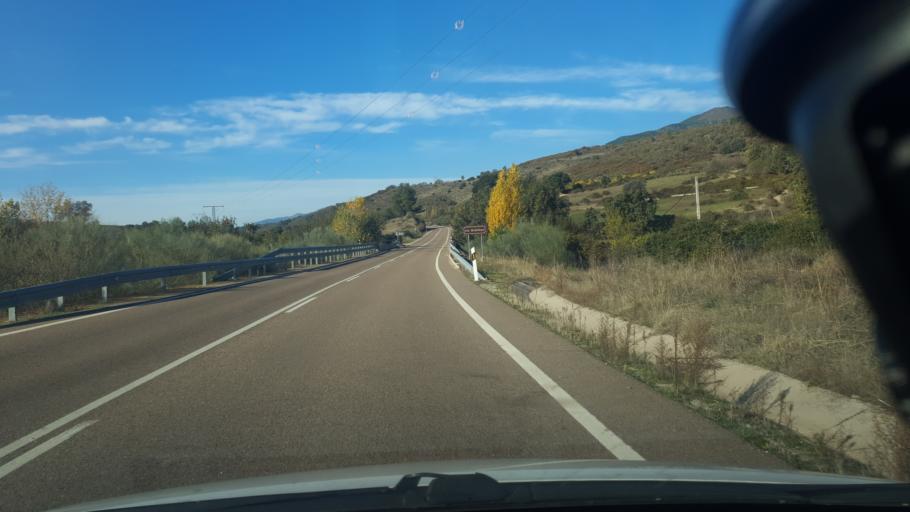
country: ES
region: Castille and Leon
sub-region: Provincia de Avila
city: Poyales del Hoyo
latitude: 40.1583
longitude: -5.1564
